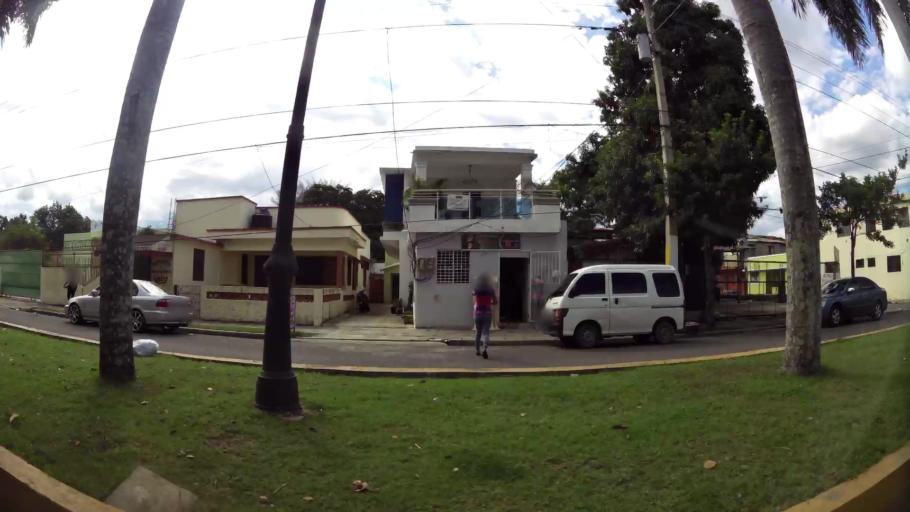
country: DO
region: La Vega
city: Concepcion de La Vega
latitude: 19.2213
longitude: -70.5308
